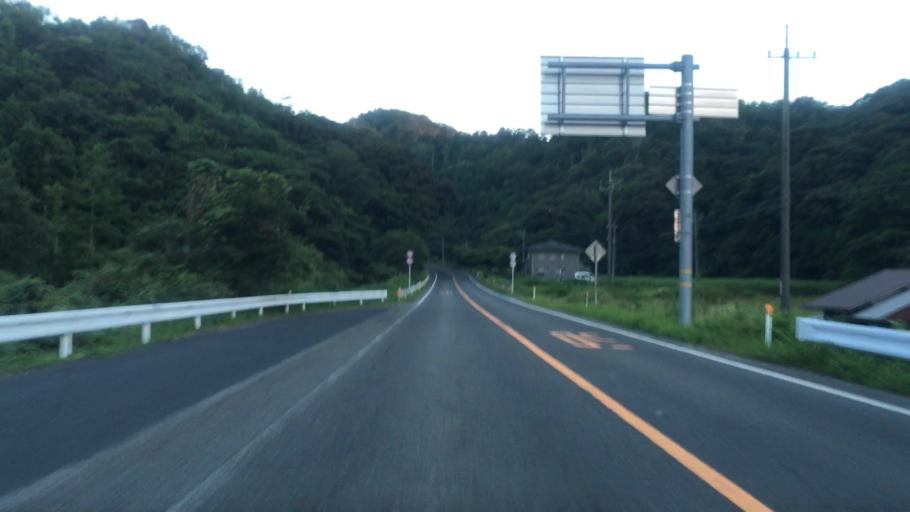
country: JP
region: Tottori
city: Tottori
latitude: 35.5986
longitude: 134.3518
